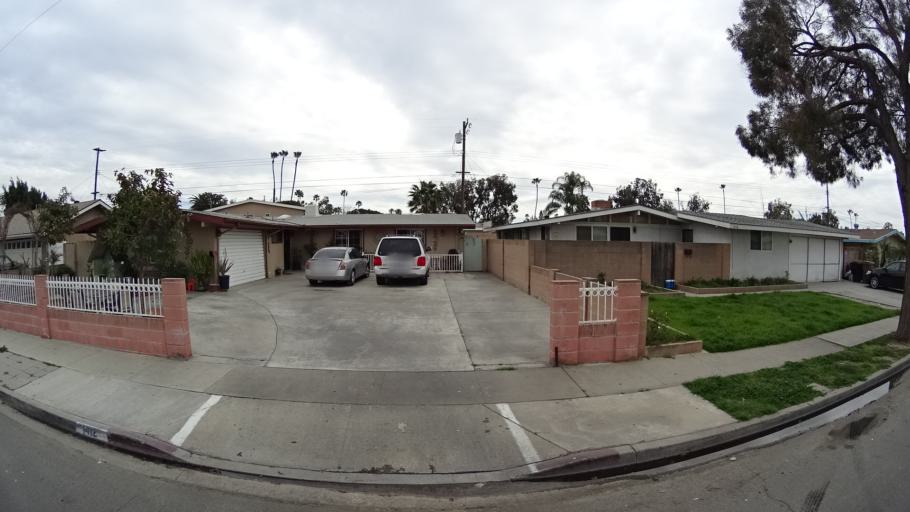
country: US
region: California
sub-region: Orange County
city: Anaheim
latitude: 33.8449
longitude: -117.9380
